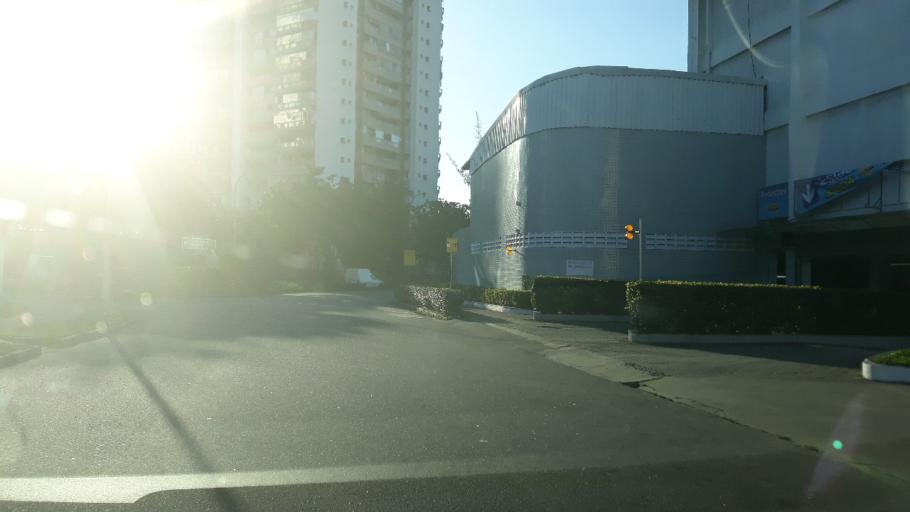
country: BR
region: Rio de Janeiro
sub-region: Rio De Janeiro
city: Rio de Janeiro
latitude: -23.0022
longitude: -43.3381
